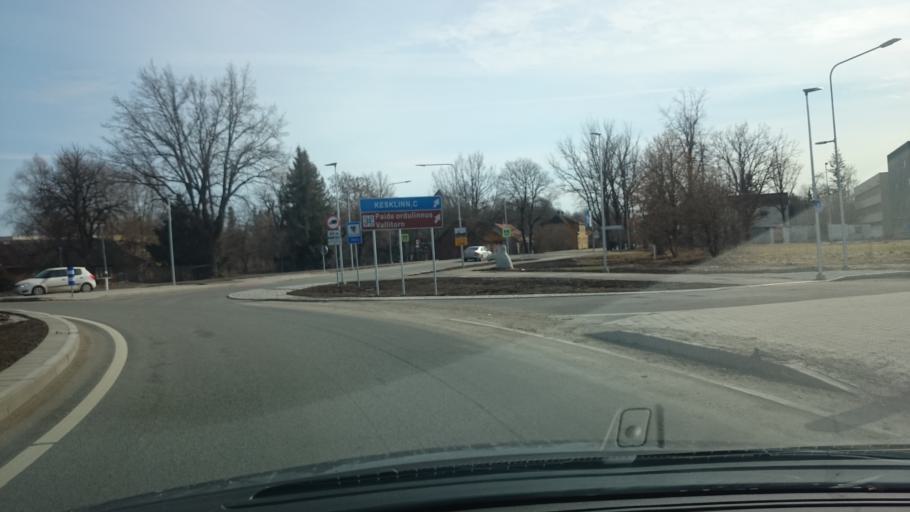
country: EE
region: Jaervamaa
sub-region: Paide linn
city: Paide
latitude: 58.8941
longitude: 25.5692
